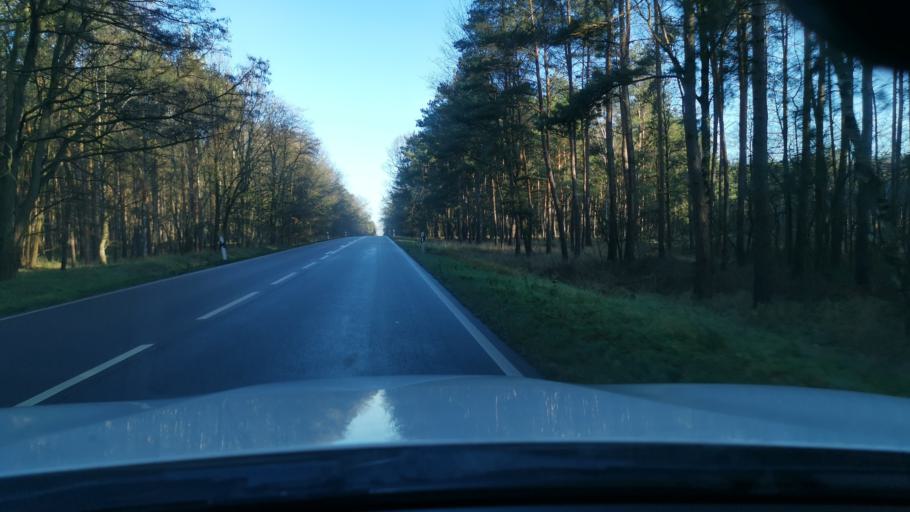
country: DE
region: Saxony-Anhalt
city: Abtsdorf
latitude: 51.9238
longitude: 12.7013
